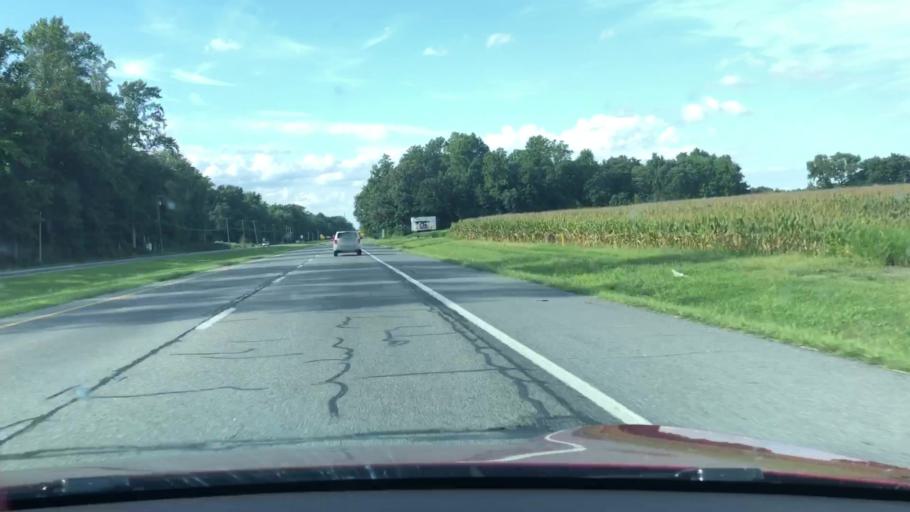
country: US
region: Delaware
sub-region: Kent County
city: Felton
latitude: 38.9666
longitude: -75.5657
